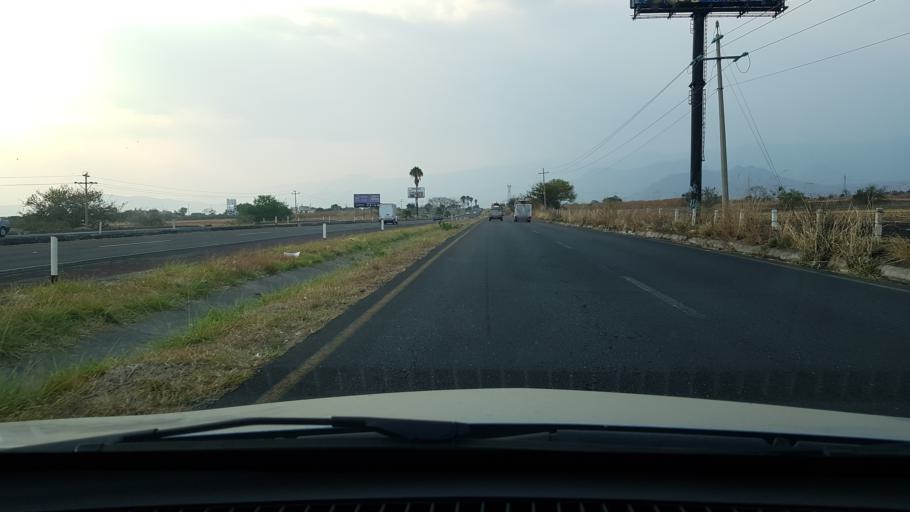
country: MX
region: Morelos
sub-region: Cuautla
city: Tierra Larga (Campo Nuevo)
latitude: 18.8702
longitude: -98.9542
